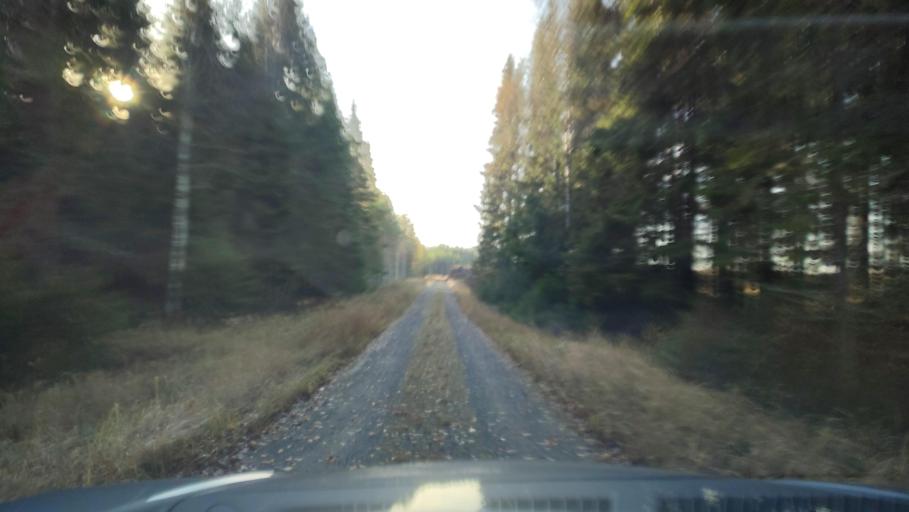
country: FI
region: Southern Ostrobothnia
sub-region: Suupohja
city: Karijoki
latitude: 62.1825
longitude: 21.6085
